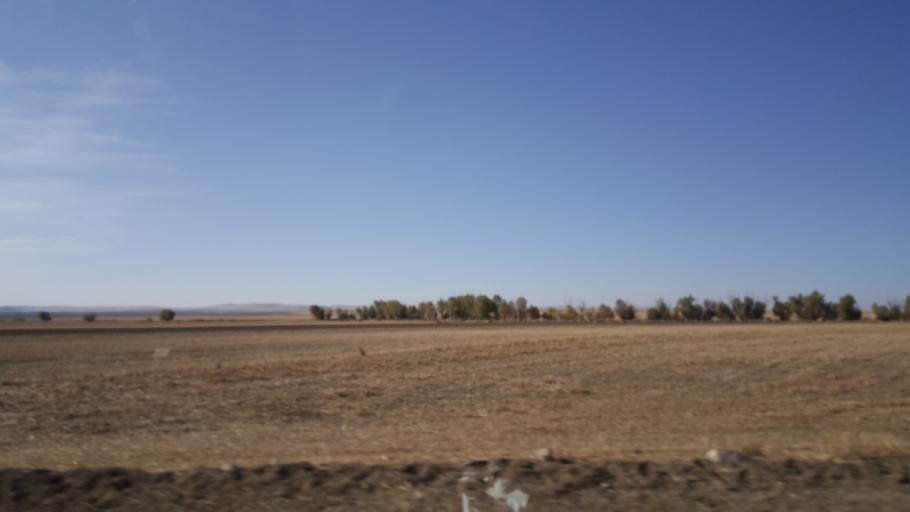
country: TR
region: Ankara
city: Yenice
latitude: 39.3755
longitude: 32.8148
